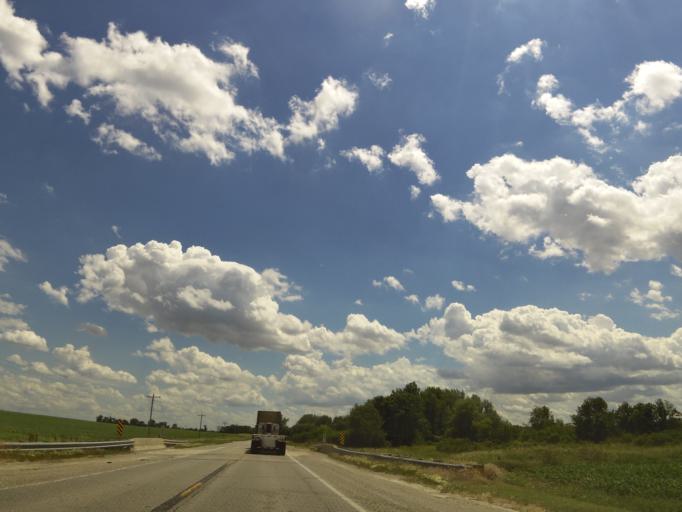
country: US
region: Iowa
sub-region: Buchanan County
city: Independence
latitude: 42.3638
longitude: -91.8893
